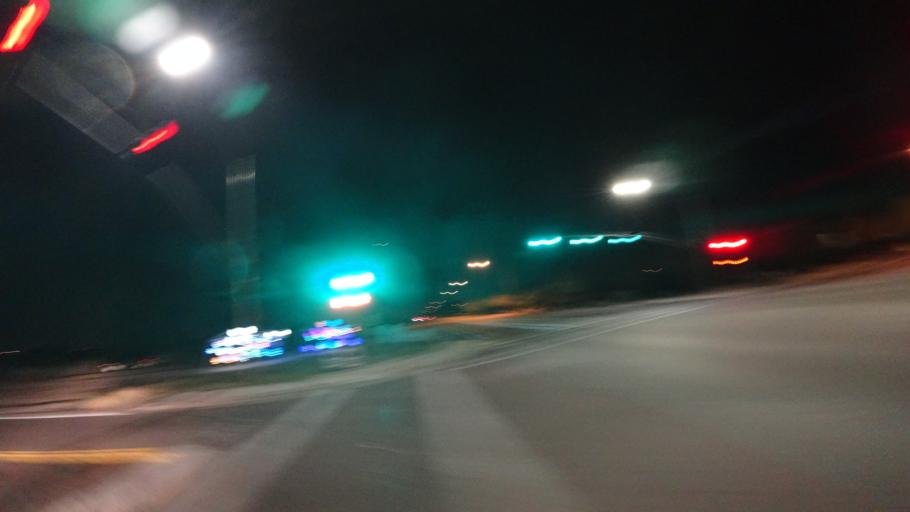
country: US
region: Arizona
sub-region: Pinal County
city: Apache Junction
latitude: 33.4368
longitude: -111.6153
